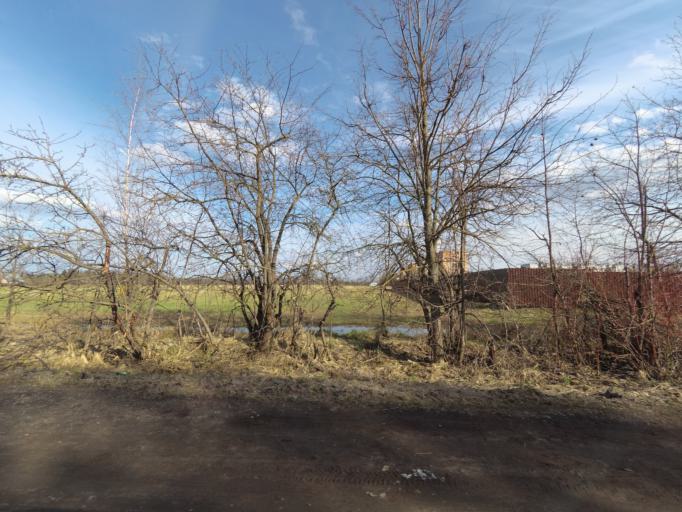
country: RU
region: Moskovskaya
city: Lugovaya
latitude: 56.0475
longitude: 37.4769
